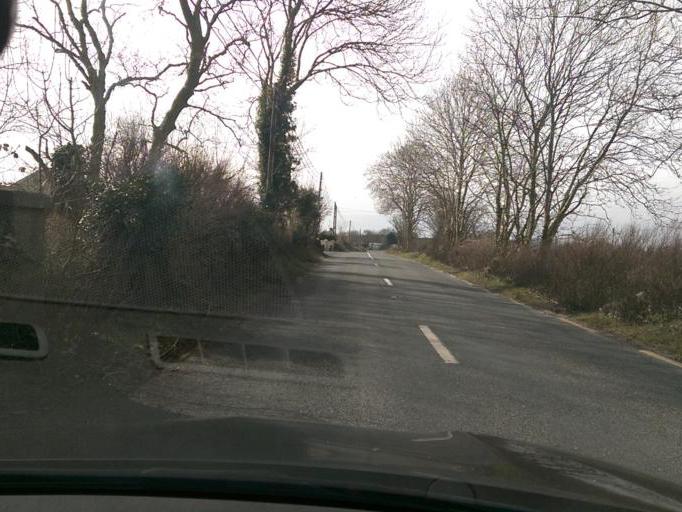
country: IE
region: Connaught
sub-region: County Galway
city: Tuam
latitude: 53.4241
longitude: -8.7822
